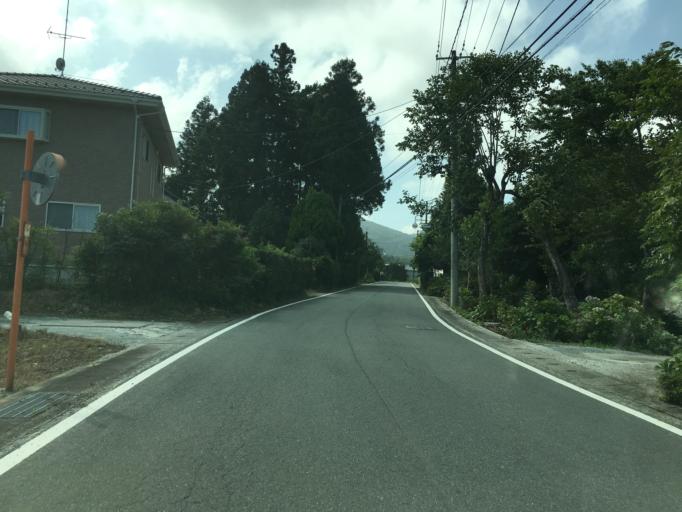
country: JP
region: Miyagi
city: Marumori
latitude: 37.8900
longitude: 140.8859
